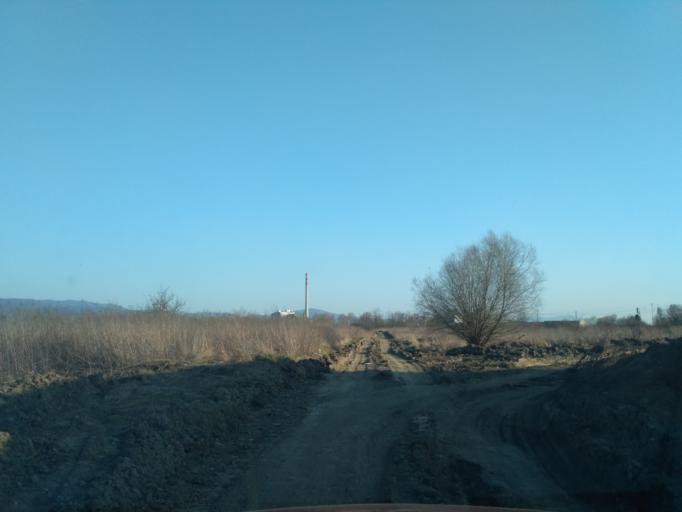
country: SK
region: Kosicky
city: Kosice
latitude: 48.6664
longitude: 21.3066
